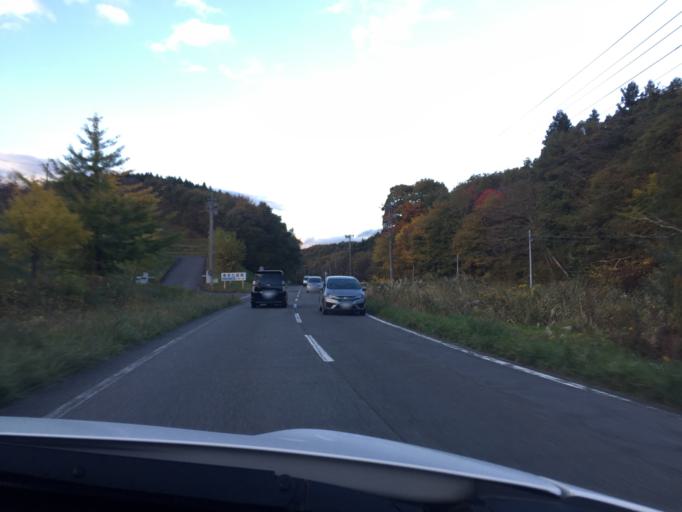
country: JP
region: Fukushima
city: Ishikawa
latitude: 37.2260
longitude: 140.6285
